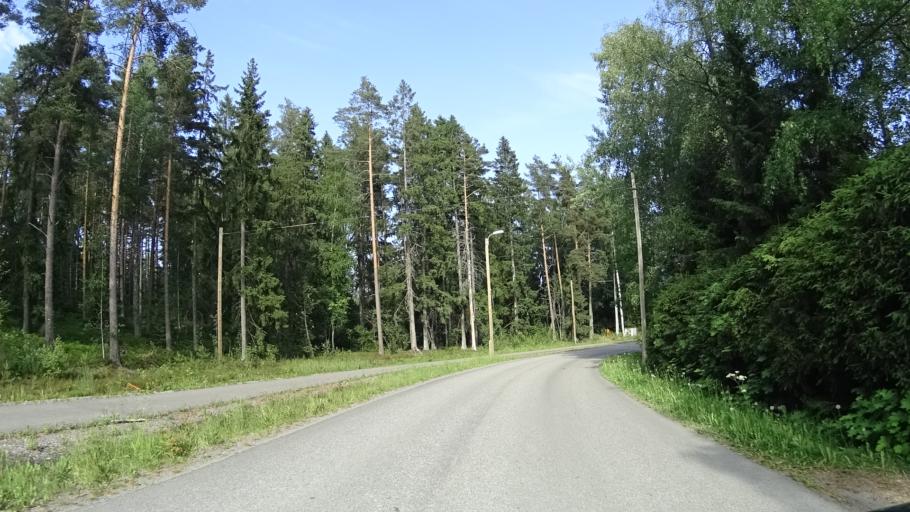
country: FI
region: Uusimaa
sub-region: Raaseporin
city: Inga
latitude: 60.0547
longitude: 23.9897
